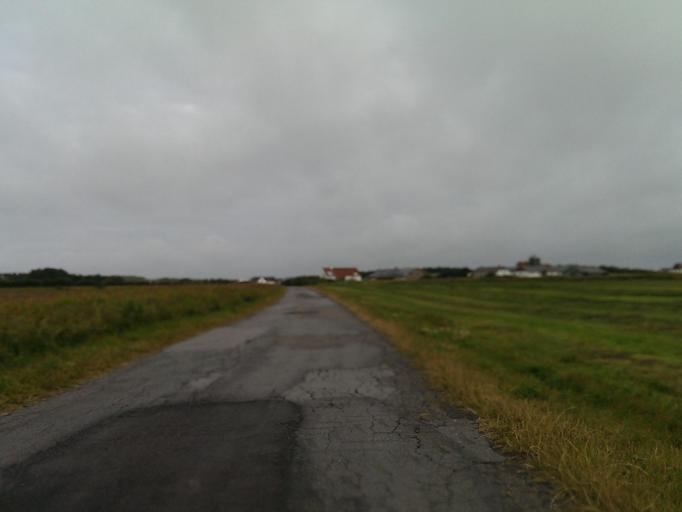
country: DK
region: North Denmark
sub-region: Jammerbugt Kommune
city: Pandrup
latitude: 57.3791
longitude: 9.7356
